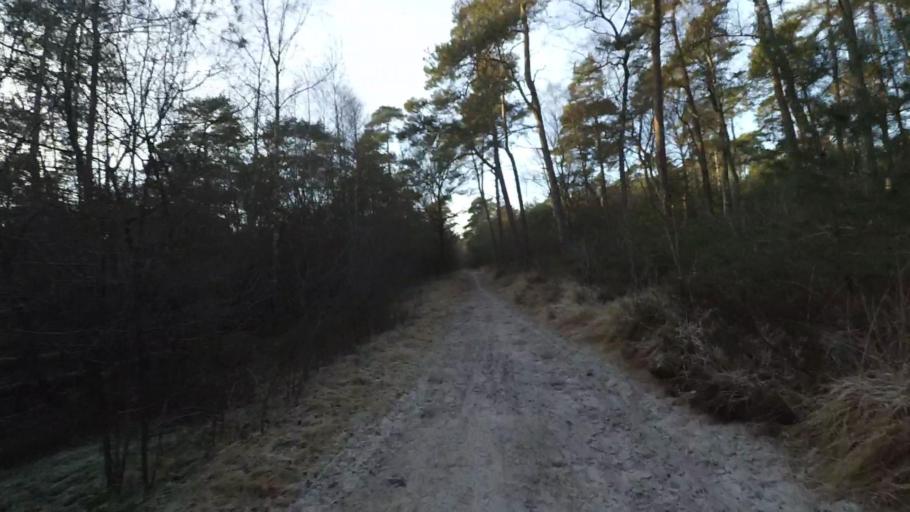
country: NL
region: Utrecht
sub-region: Gemeente Utrechtse Heuvelrug
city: Maarn
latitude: 52.0885
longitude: 5.3526
